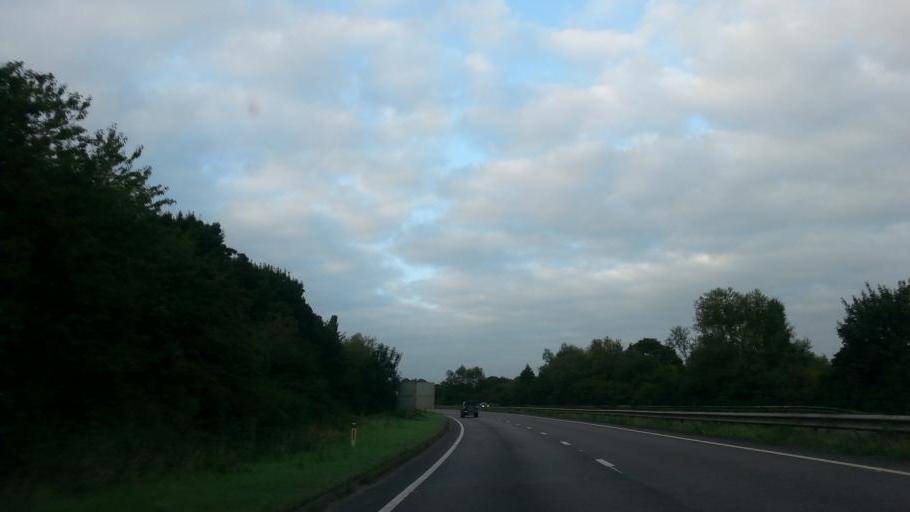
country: GB
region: England
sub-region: Northamptonshire
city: Brackley
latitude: 52.0229
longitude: -1.1378
